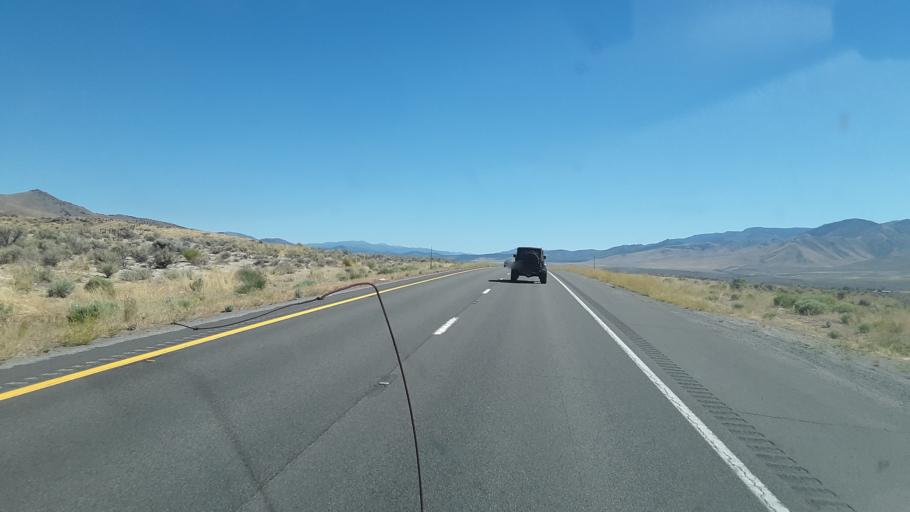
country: US
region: Nevada
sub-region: Washoe County
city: Cold Springs
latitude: 39.7614
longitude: -120.0392
